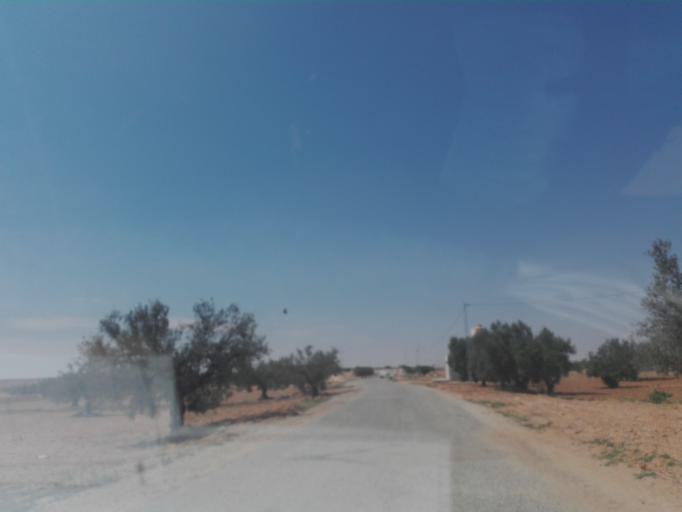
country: TN
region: Safaqis
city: Bi'r `Ali Bin Khalifah
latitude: 34.6245
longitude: 10.3689
